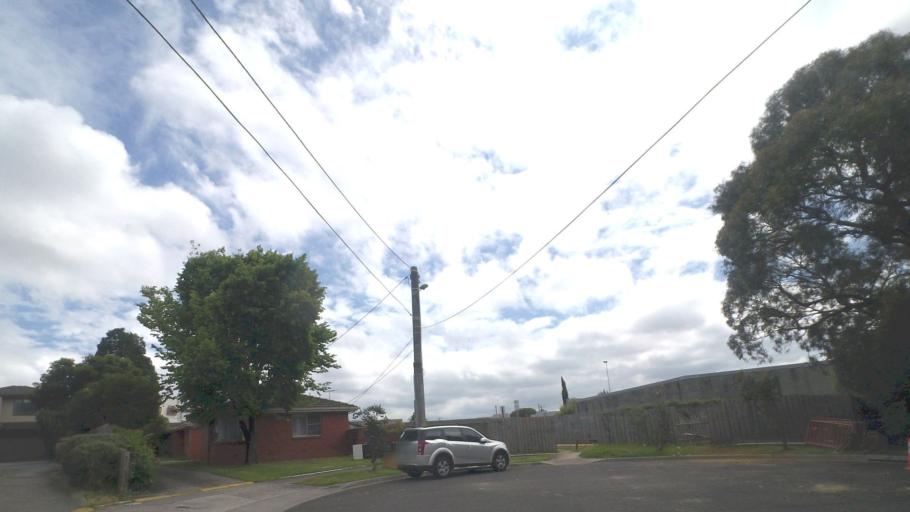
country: AU
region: Victoria
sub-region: Knox
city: Bayswater
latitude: -37.8435
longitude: 145.2654
